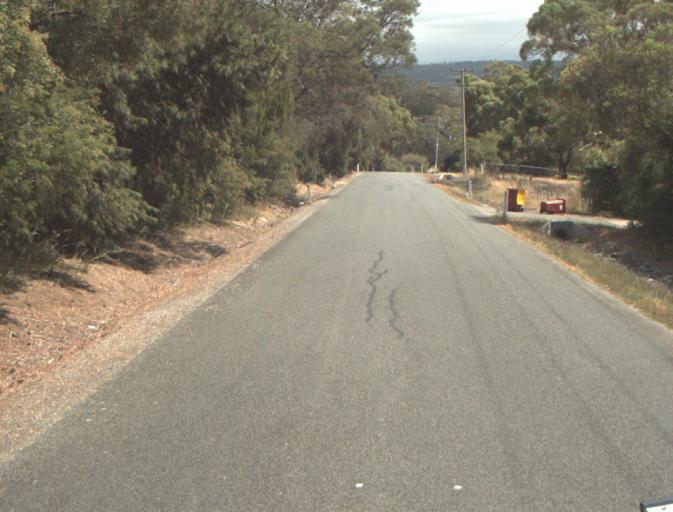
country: AU
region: Tasmania
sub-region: Launceston
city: Newstead
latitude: -41.4481
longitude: 147.2102
